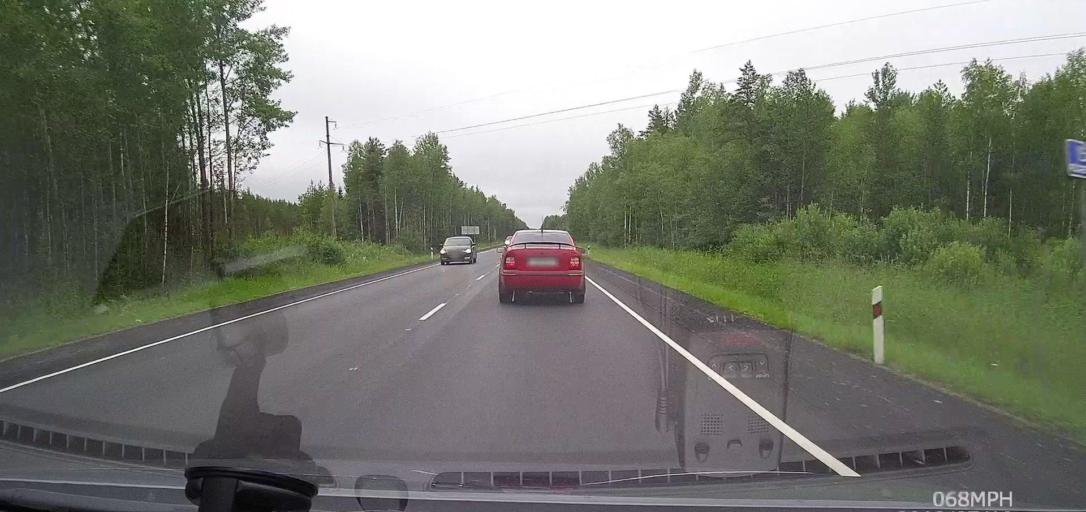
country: RU
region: Leningrad
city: Syas'stroy
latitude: 60.2490
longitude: 32.7592
